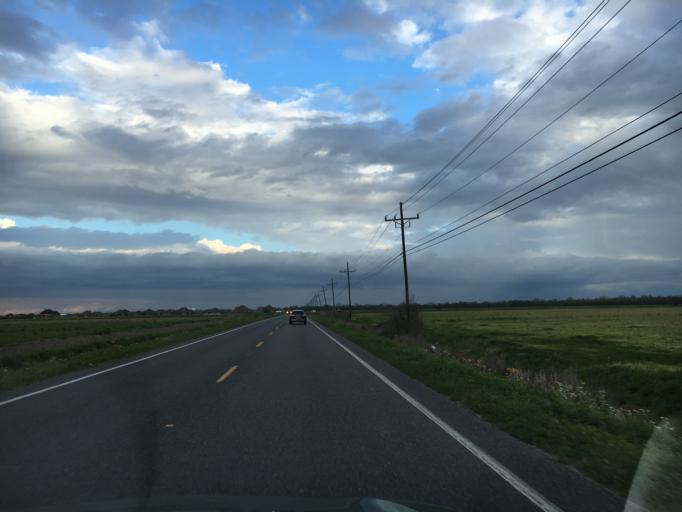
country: US
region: Louisiana
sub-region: West Baton Rouge Parish
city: Brusly
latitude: 30.4685
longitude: -91.3118
